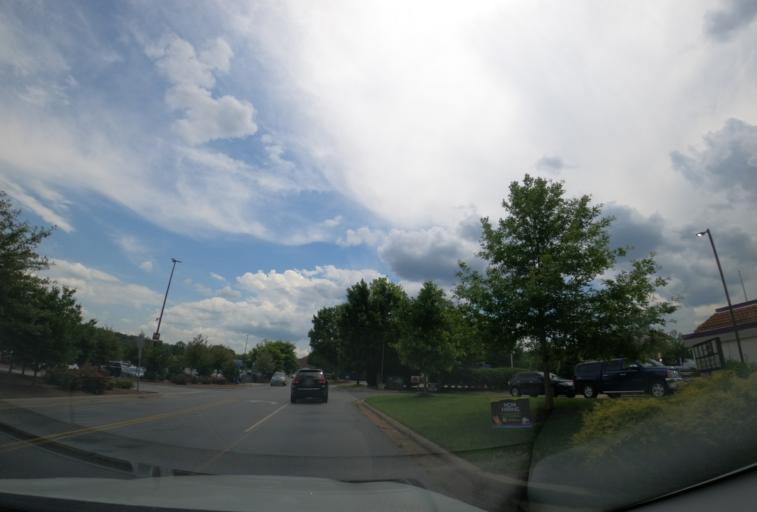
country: US
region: North Carolina
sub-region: Buncombe County
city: Bent Creek
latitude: 35.5294
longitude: -82.6052
